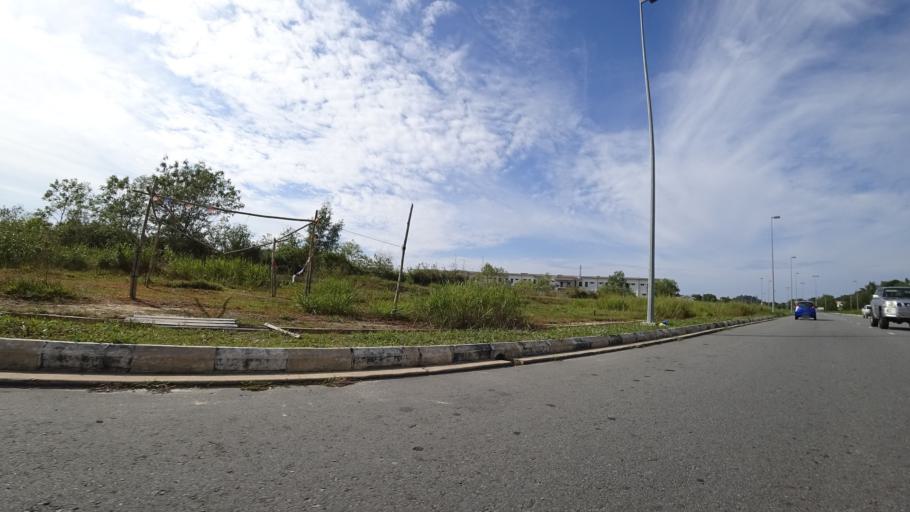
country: BN
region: Brunei and Muara
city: Bandar Seri Begawan
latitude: 4.8901
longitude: 114.8033
